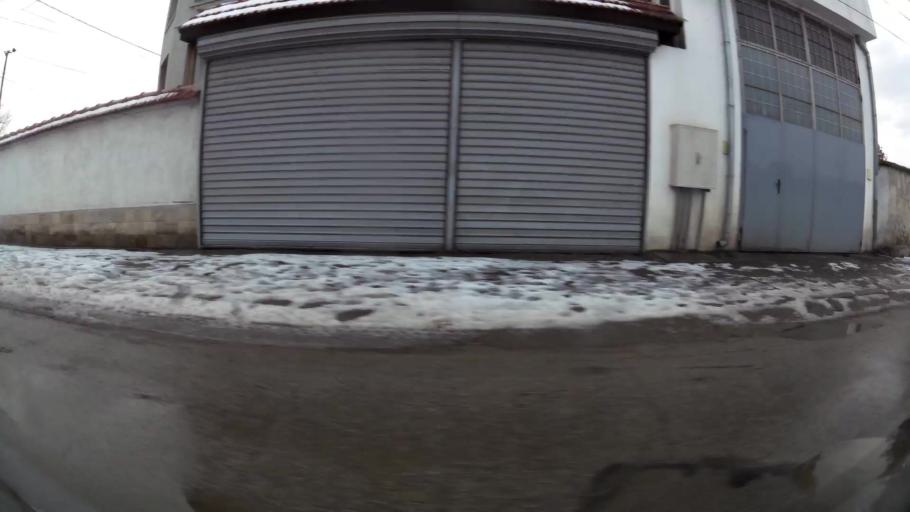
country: BG
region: Sofia-Capital
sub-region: Stolichna Obshtina
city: Sofia
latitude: 42.7242
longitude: 23.3468
